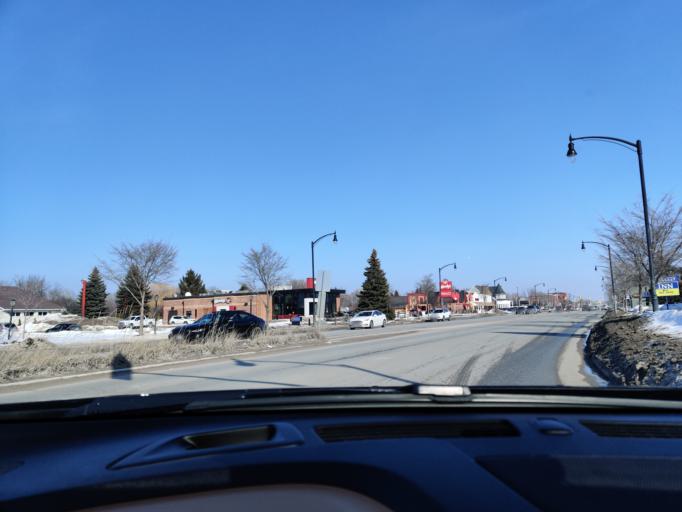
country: CA
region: Ontario
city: Collingwood
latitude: 44.5011
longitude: -80.2342
